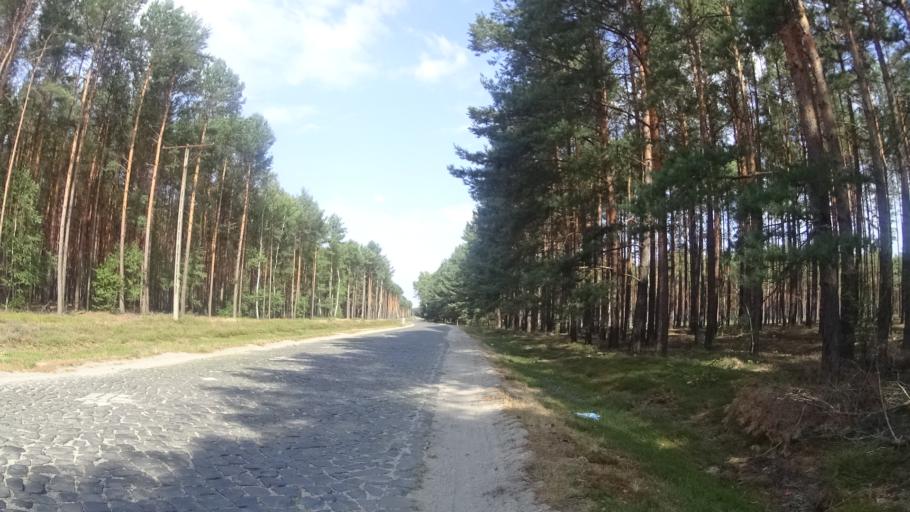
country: PL
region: Lubusz
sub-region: Powiat zarski
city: Leknica
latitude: 51.5115
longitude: 14.8351
